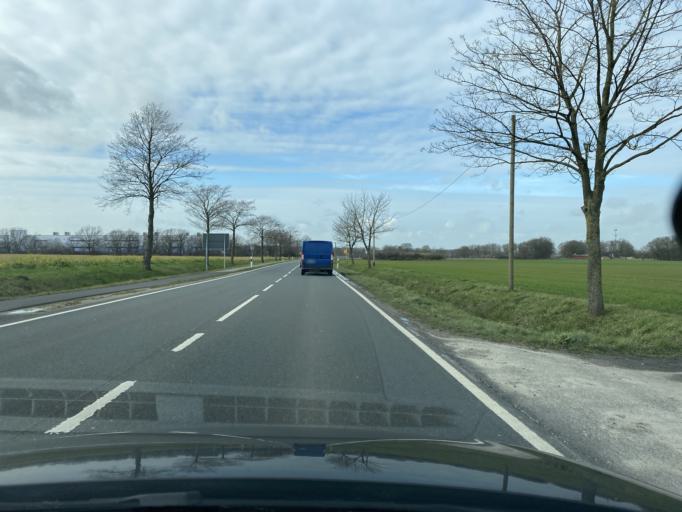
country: DE
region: North Rhine-Westphalia
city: Oelde
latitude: 51.8347
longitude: 8.2114
